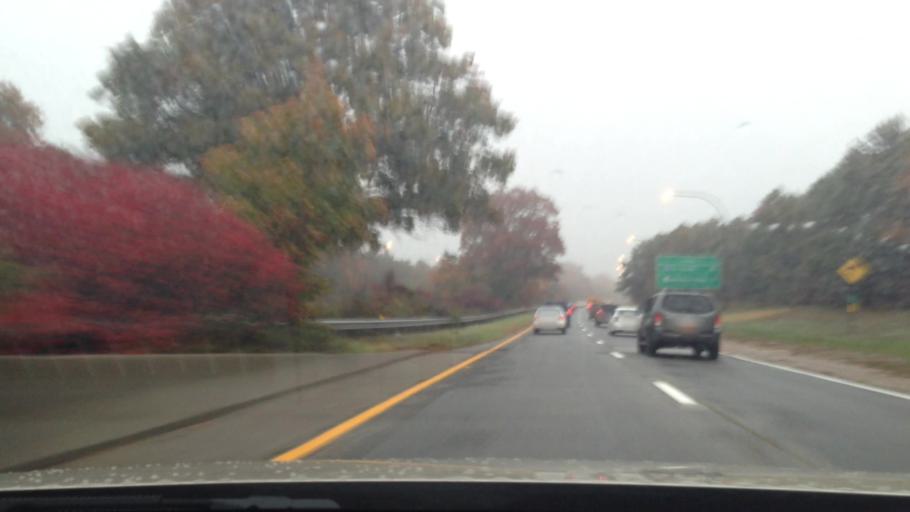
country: US
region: New York
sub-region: Suffolk County
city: Bay Wood
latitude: 40.7758
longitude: -73.2803
